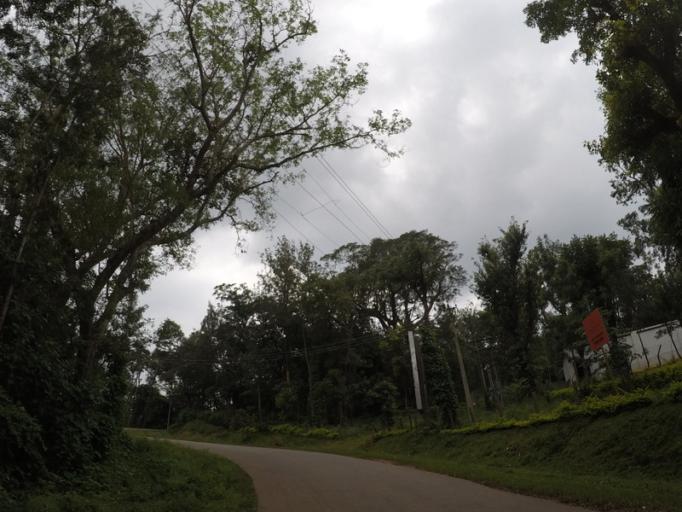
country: IN
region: Karnataka
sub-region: Chikmagalur
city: Chikmagalur
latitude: 13.4719
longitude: 75.7990
